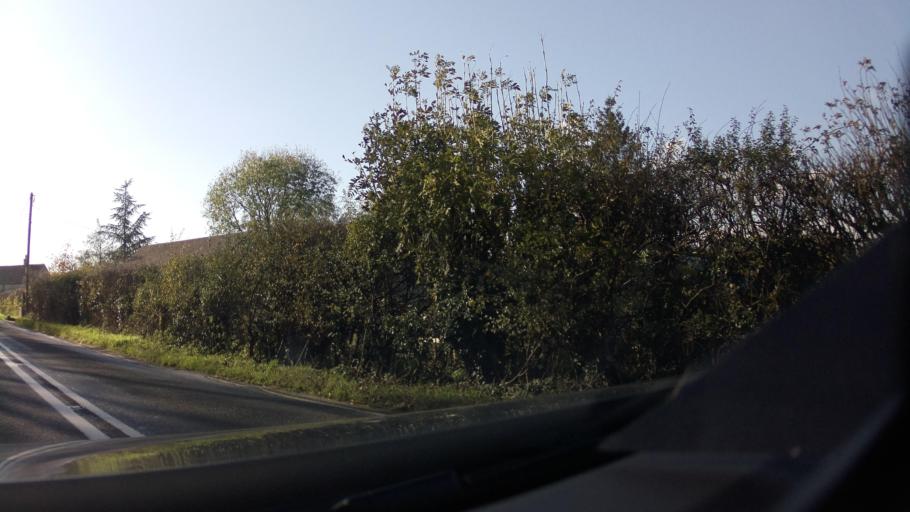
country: GB
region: England
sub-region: Somerset
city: Frome
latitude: 51.1985
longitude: -2.3207
